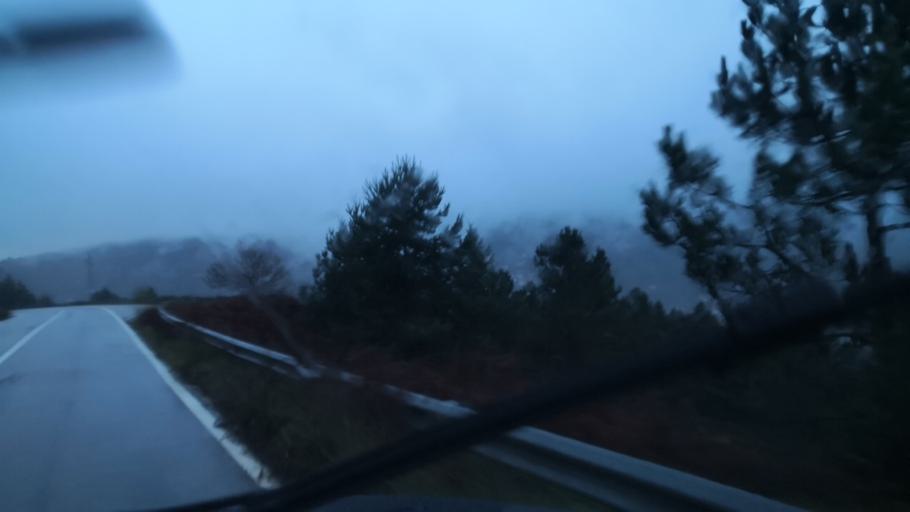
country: PT
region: Vila Real
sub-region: Vila Pouca de Aguiar
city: Vila Pouca de Aguiar
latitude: 41.5016
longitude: -7.6324
